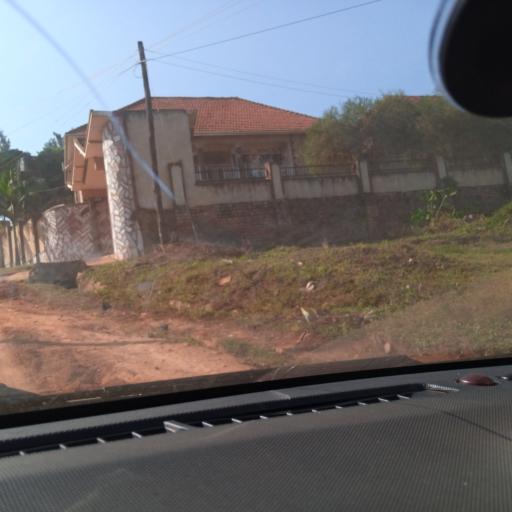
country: UG
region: Central Region
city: Masaka
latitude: -0.3334
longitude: 31.7351
